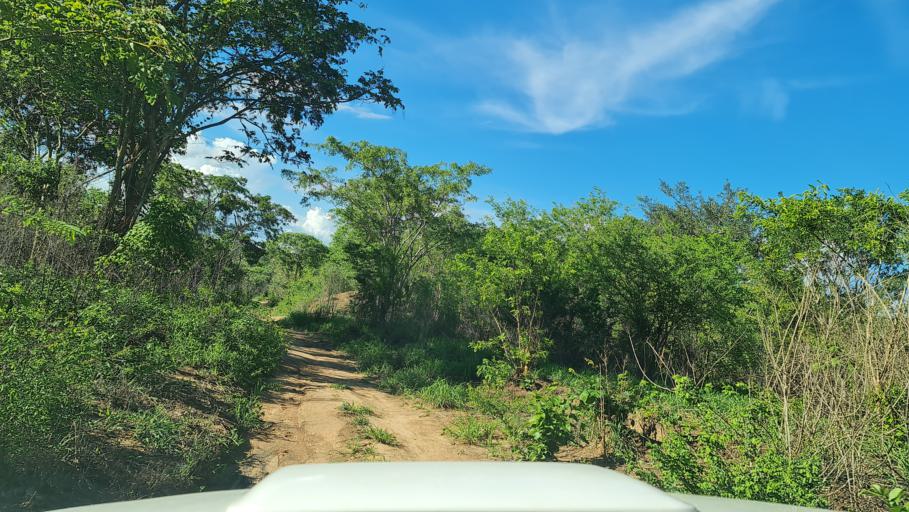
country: MZ
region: Nampula
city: Ilha de Mocambique
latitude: -15.2585
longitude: 40.1842
